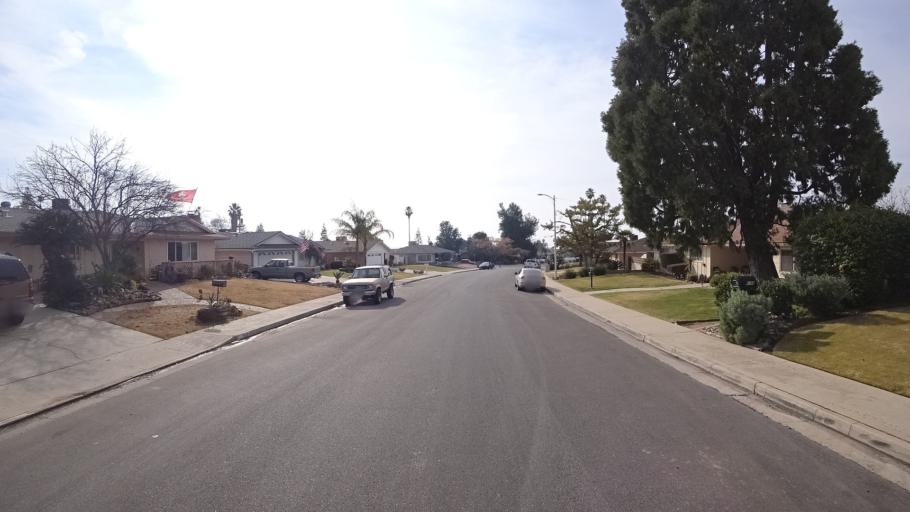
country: US
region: California
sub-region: Kern County
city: Oildale
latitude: 35.4018
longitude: -118.9510
